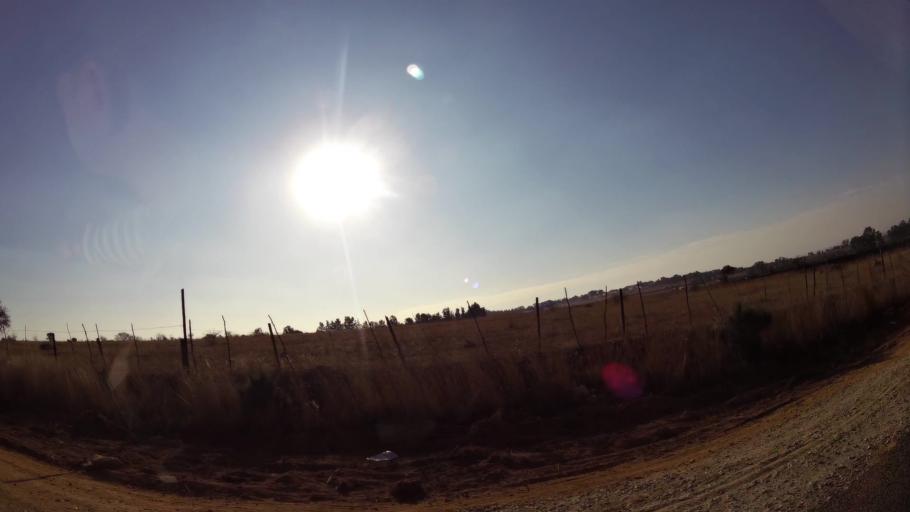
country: ZA
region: Gauteng
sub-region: West Rand District Municipality
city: Muldersdriseloop
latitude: -26.0097
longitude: 27.8949
